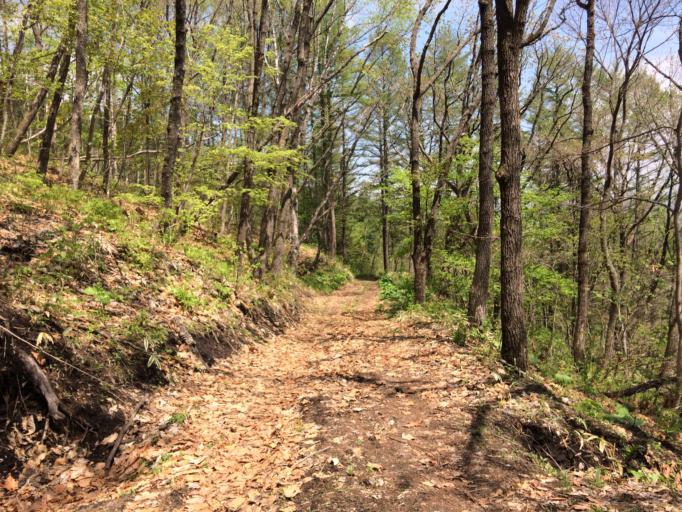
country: JP
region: Hokkaido
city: Obihiro
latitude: 42.9409
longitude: 143.4197
